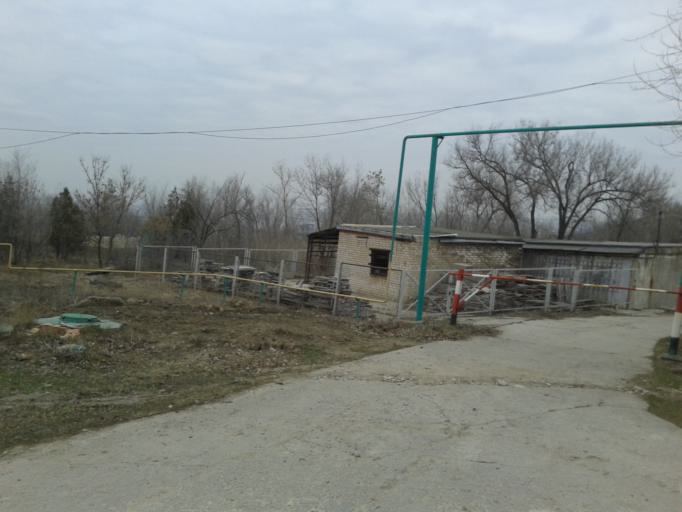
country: RU
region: Volgograd
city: Volgograd
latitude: 48.7430
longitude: 44.5368
